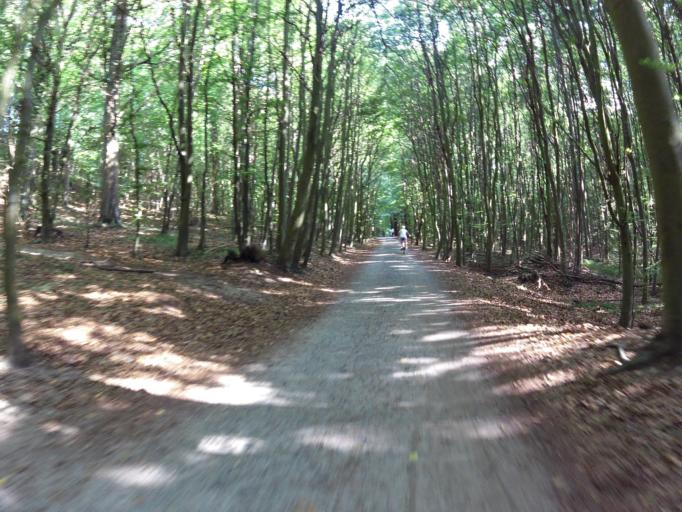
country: DE
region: Mecklenburg-Vorpommern
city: Koserow
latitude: 54.0509
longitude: 14.0145
